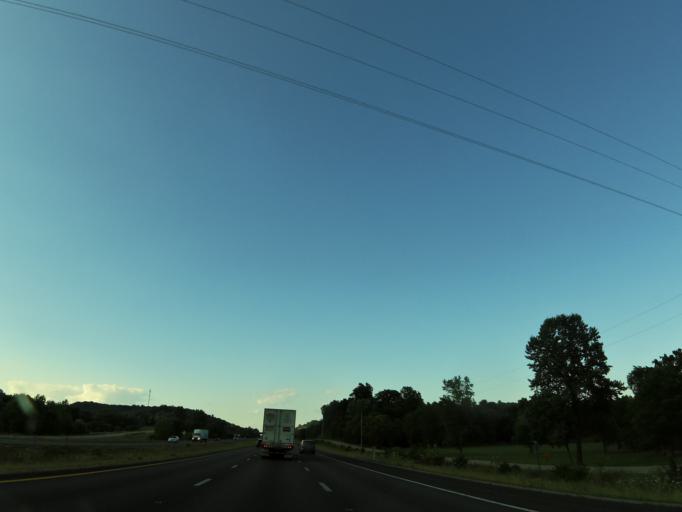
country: US
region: Tennessee
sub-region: Williamson County
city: Thompson's Station
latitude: 35.8108
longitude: -86.8463
